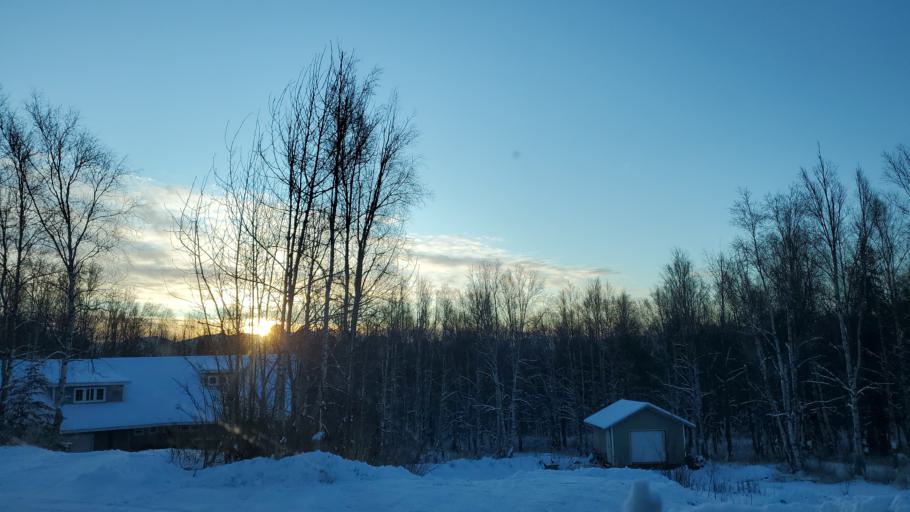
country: US
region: Alaska
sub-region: Matanuska-Susitna Borough
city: Lakes
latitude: 61.6365
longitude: -149.3093
